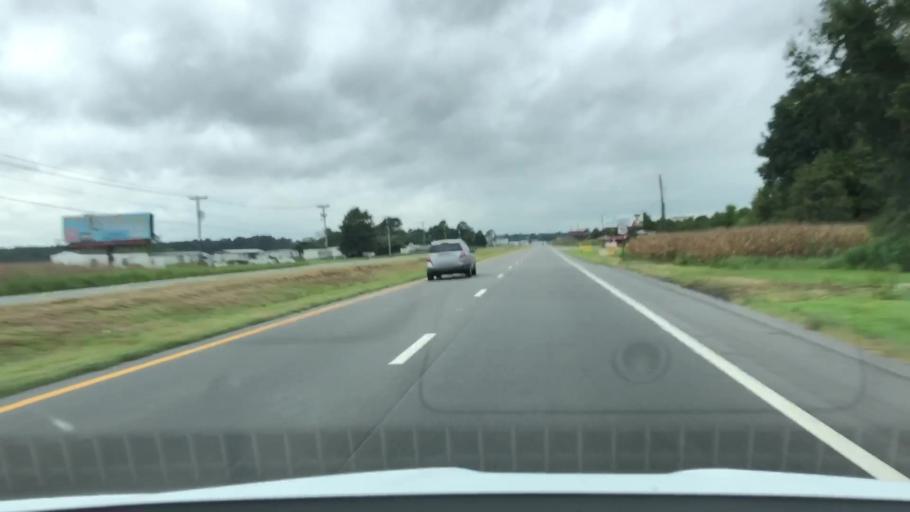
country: US
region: North Carolina
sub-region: Lenoir County
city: La Grange
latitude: 35.2646
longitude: -77.7248
